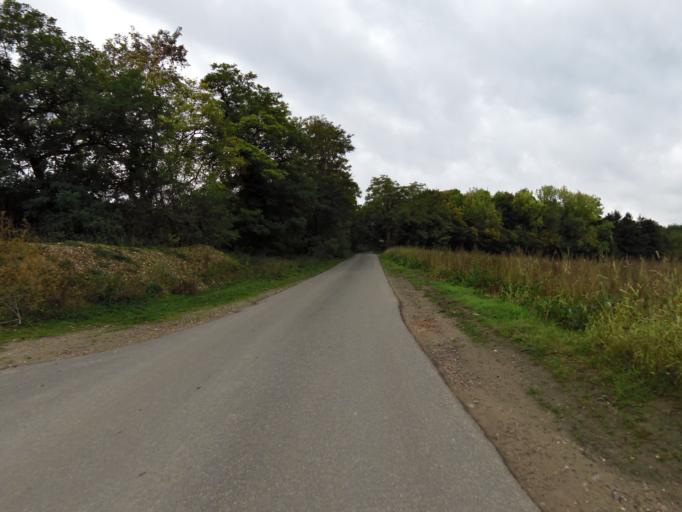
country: DE
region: Rheinland-Pfalz
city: Morstadt
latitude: 49.6657
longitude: 8.2852
